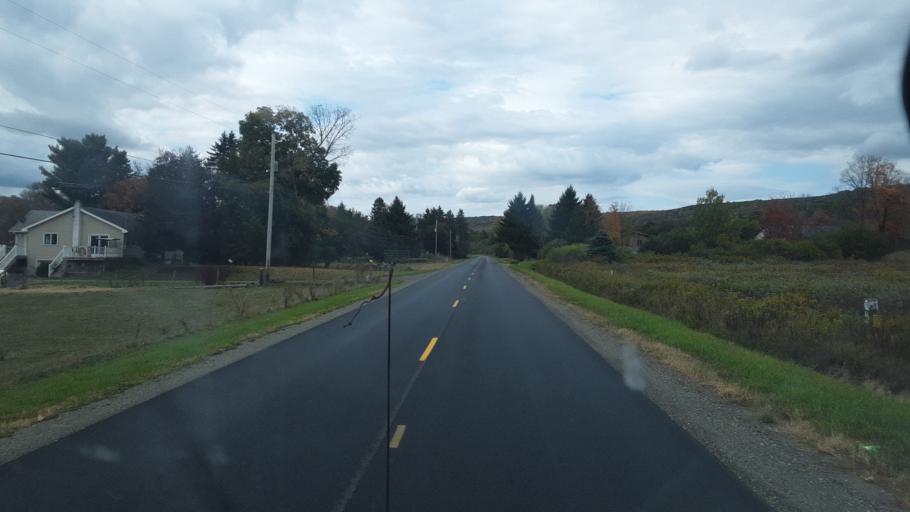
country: US
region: New York
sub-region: Allegany County
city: Alfred
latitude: 42.3682
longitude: -77.7877
